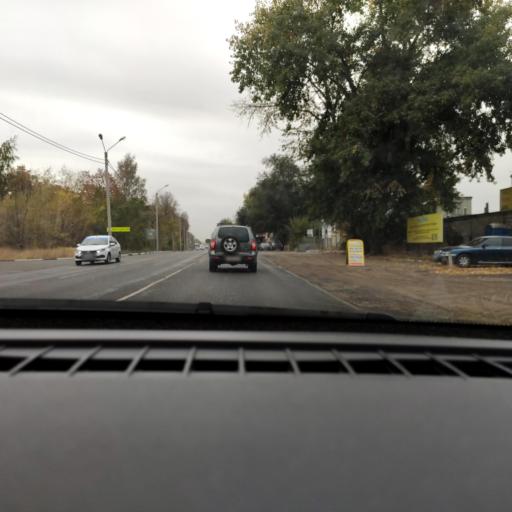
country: RU
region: Voronezj
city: Voronezh
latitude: 51.6716
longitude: 39.2719
